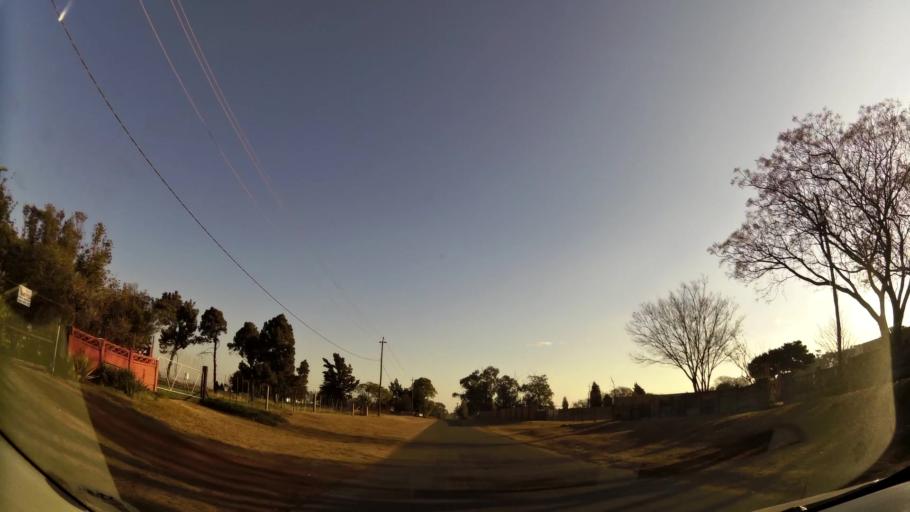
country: ZA
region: Gauteng
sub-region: West Rand District Municipality
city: Randfontein
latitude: -26.2148
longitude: 27.6554
